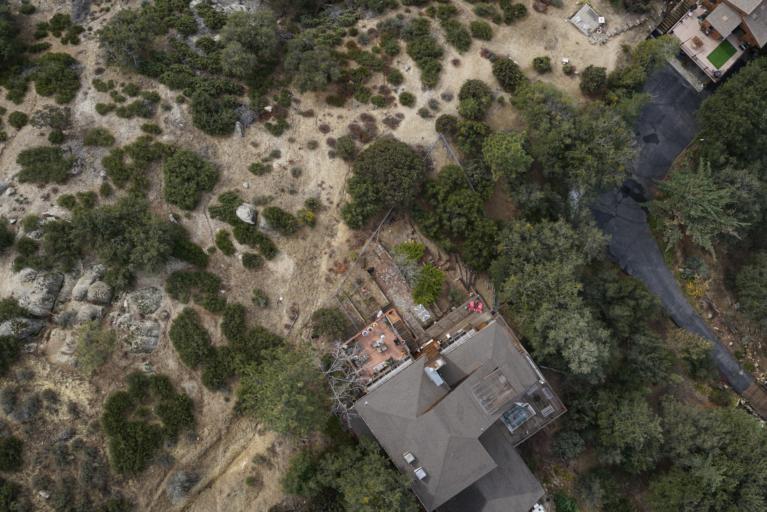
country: US
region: California
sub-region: Riverside County
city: Idyllwild
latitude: 33.7263
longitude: -116.7147
